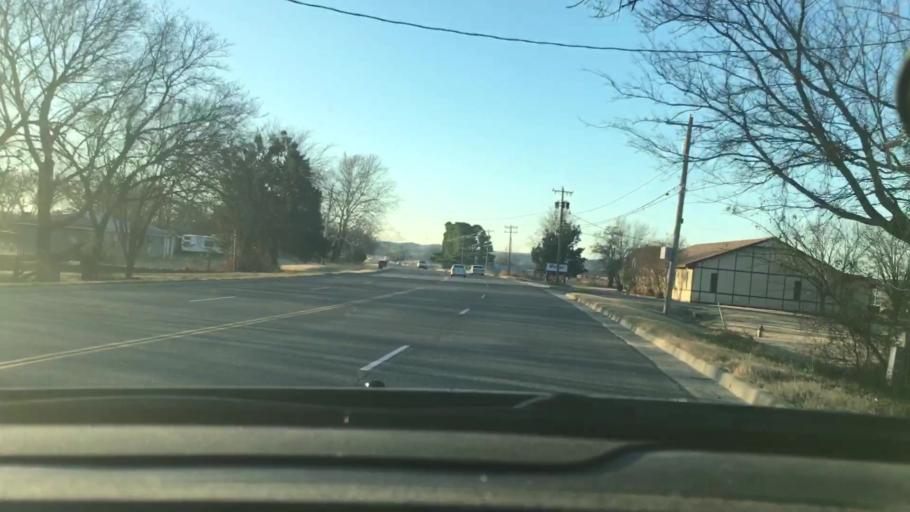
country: US
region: Oklahoma
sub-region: Murray County
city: Davis
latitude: 34.4754
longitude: -97.1318
